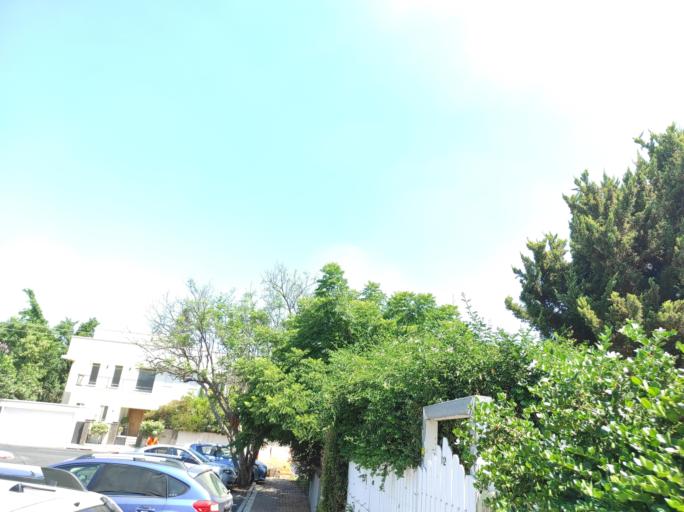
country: IL
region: Central District
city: Yehud
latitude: 32.0265
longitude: 34.8783
